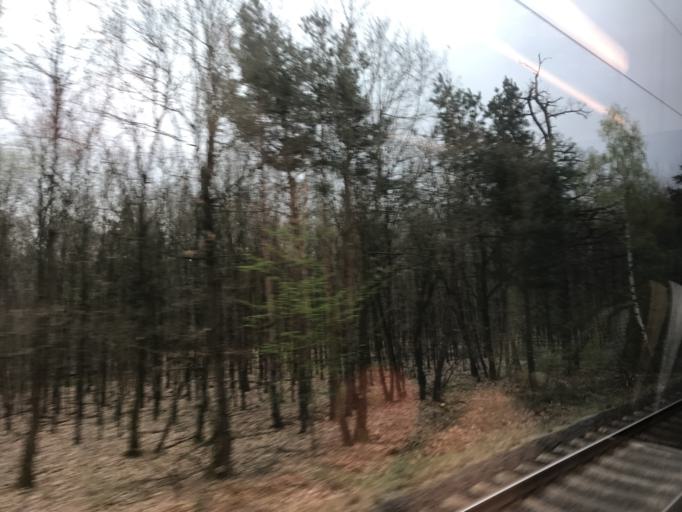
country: DE
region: Hesse
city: Kelsterbach
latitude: 50.0610
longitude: 8.5515
